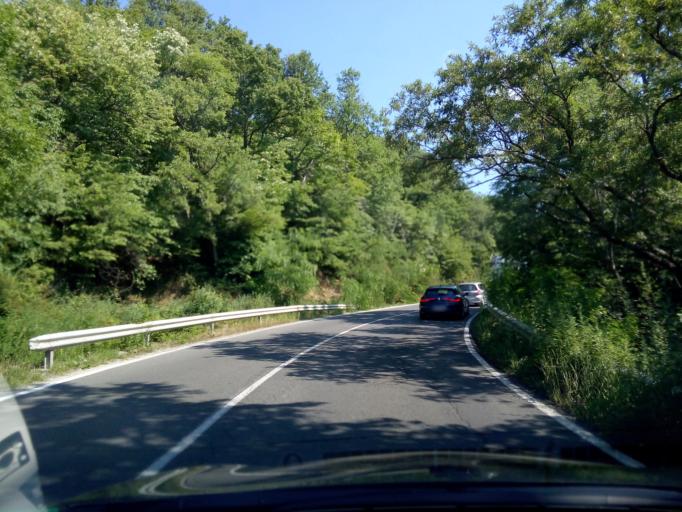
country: BG
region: Burgas
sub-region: Obshtina Nesebur
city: Sveti Vlas
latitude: 42.7345
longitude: 27.7386
